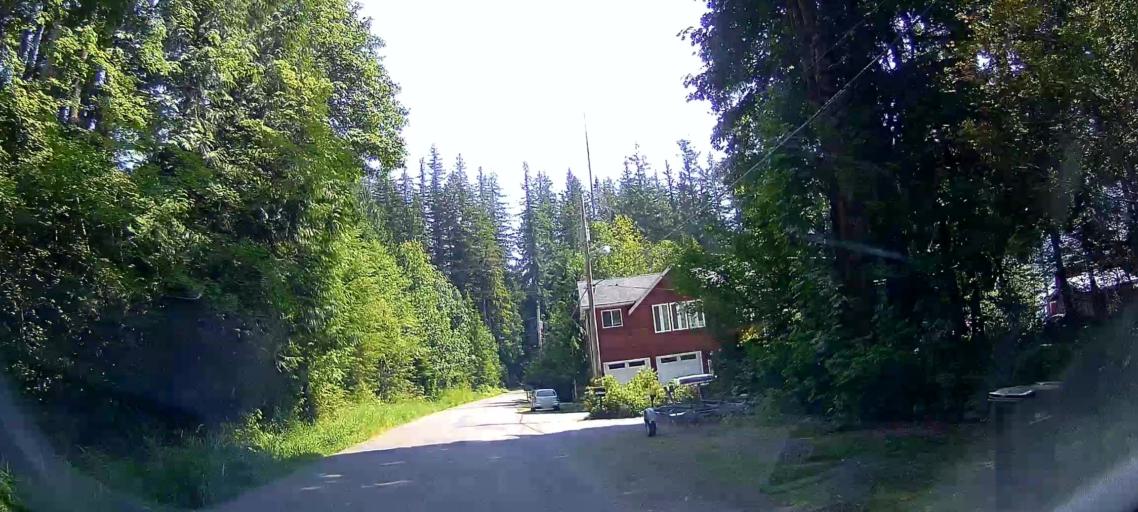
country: US
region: Washington
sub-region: Snohomish County
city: Arlington Heights
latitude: 48.3295
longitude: -122.0101
